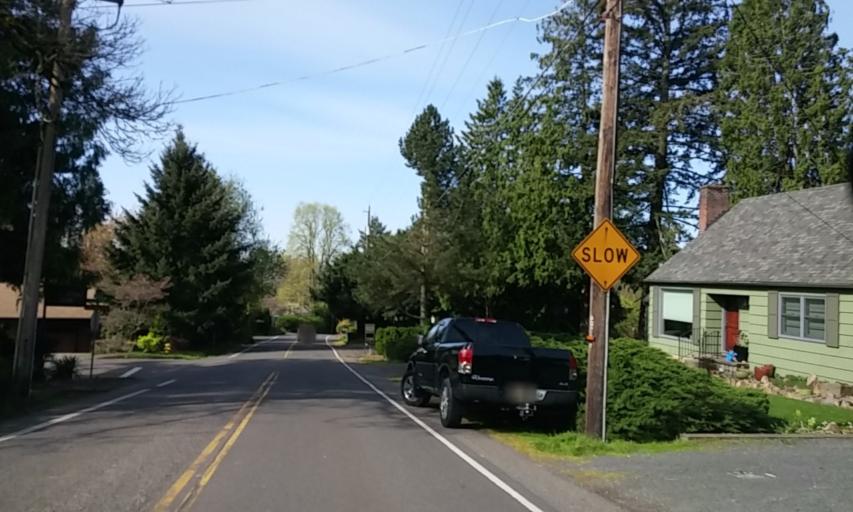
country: US
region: Oregon
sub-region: Washington County
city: West Slope
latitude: 45.5012
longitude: -122.7576
